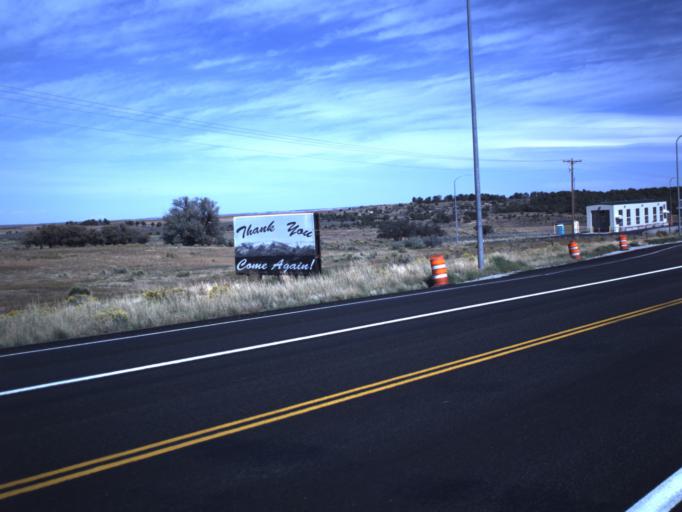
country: US
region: Utah
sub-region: San Juan County
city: Monticello
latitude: 37.8728
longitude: -109.3097
